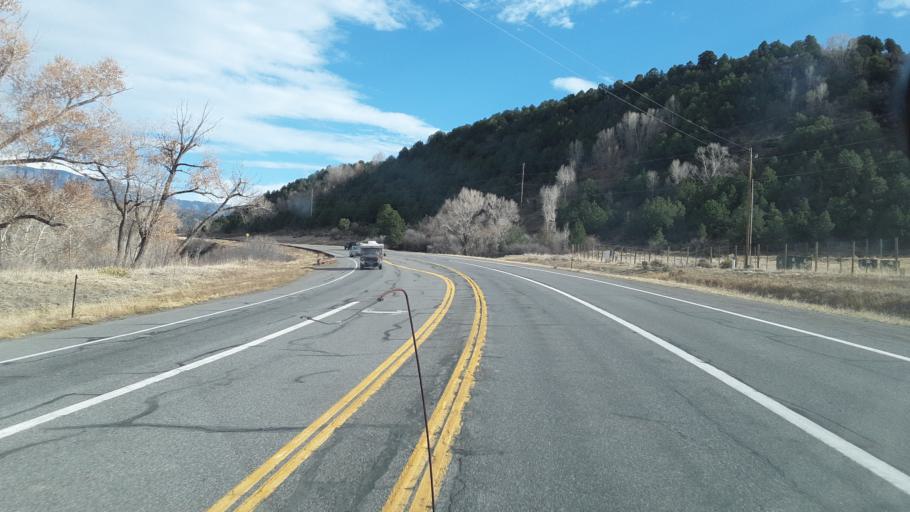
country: US
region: Colorado
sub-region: Ouray County
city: Ouray
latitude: 38.2455
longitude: -107.7583
